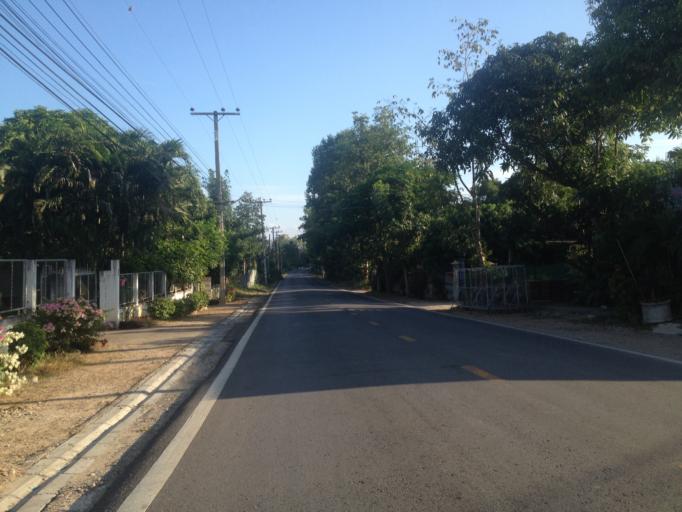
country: TH
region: Chiang Mai
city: San Pa Tong
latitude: 18.5840
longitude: 98.8644
